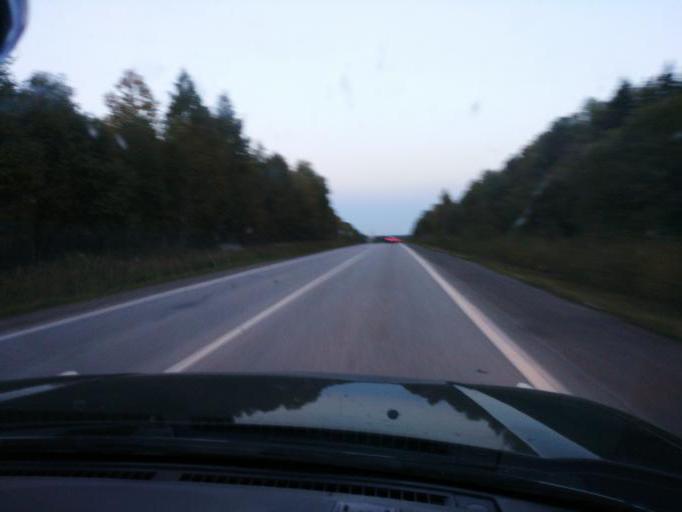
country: RU
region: Perm
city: Verkhnechusovskiye Gorodki
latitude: 58.2613
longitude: 56.9782
